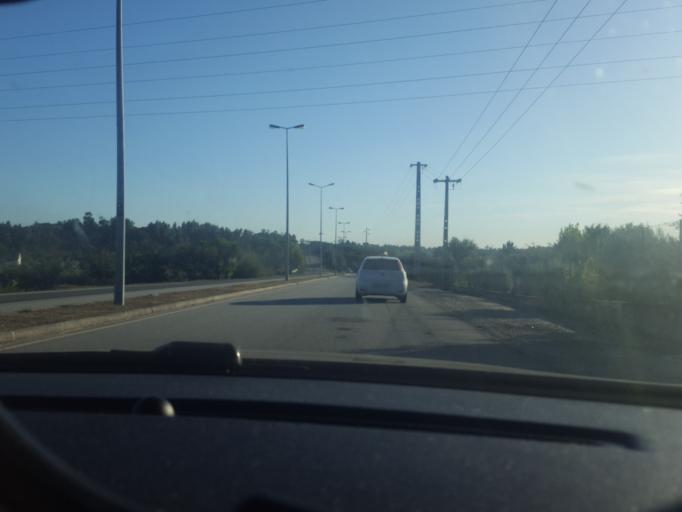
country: PT
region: Viseu
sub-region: Nelas
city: Nelas
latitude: 40.5365
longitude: -7.8601
